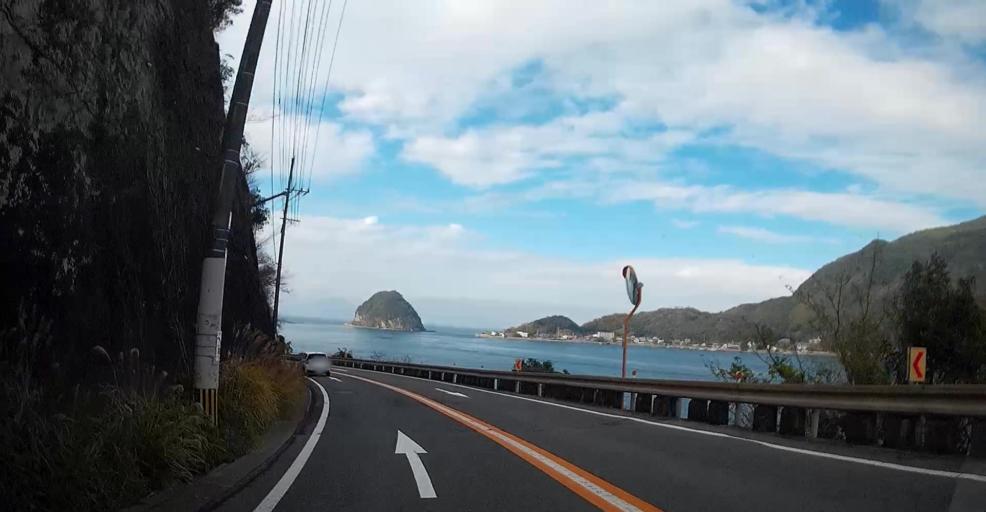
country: JP
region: Kumamoto
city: Yatsushiro
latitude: 32.6152
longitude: 130.4541
